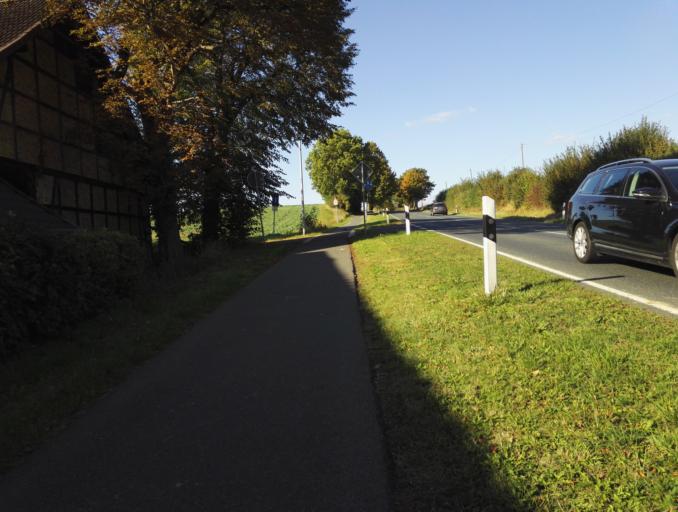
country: DE
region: Lower Saxony
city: Holle
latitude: 52.1090
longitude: 10.1084
